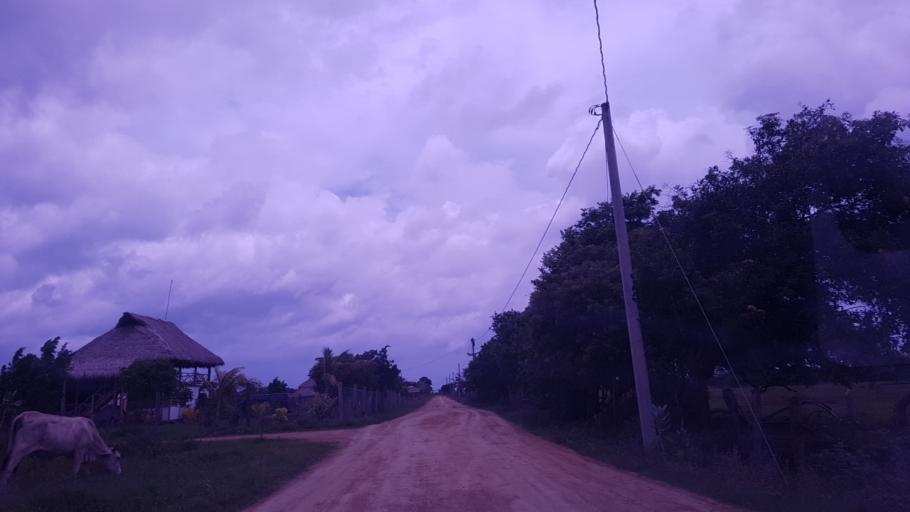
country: NI
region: Rivas
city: Tola
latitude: 11.4512
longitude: -86.0920
